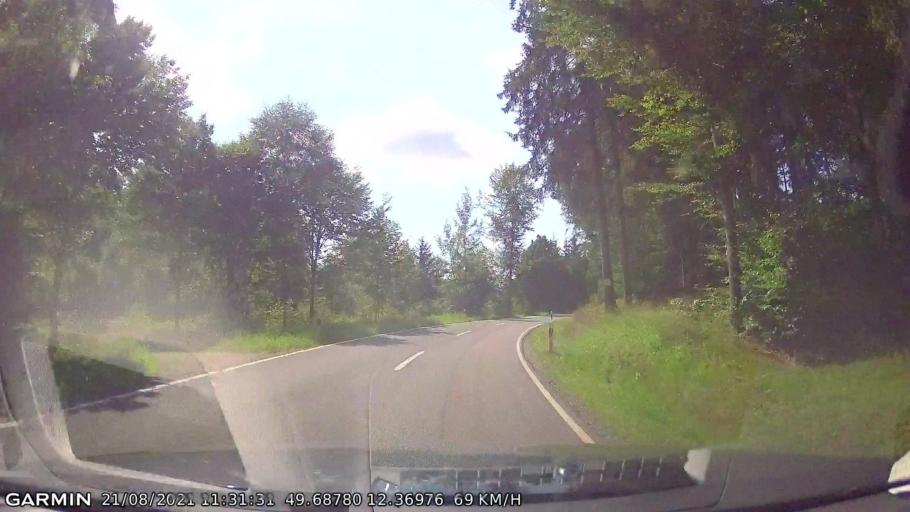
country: DE
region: Bavaria
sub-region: Upper Palatinate
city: Waldthurn
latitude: 49.6876
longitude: 12.3698
